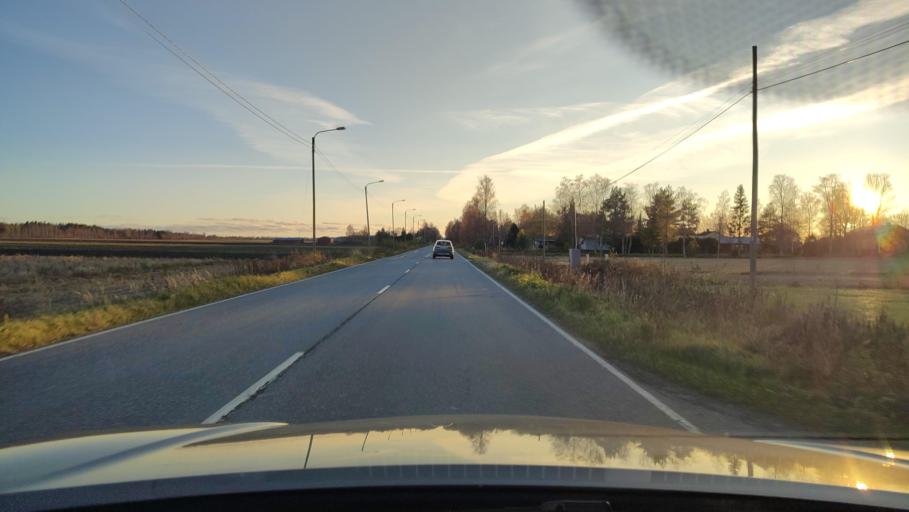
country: FI
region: Ostrobothnia
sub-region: Sydosterbotten
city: Naerpes
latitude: 62.5099
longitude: 21.3596
